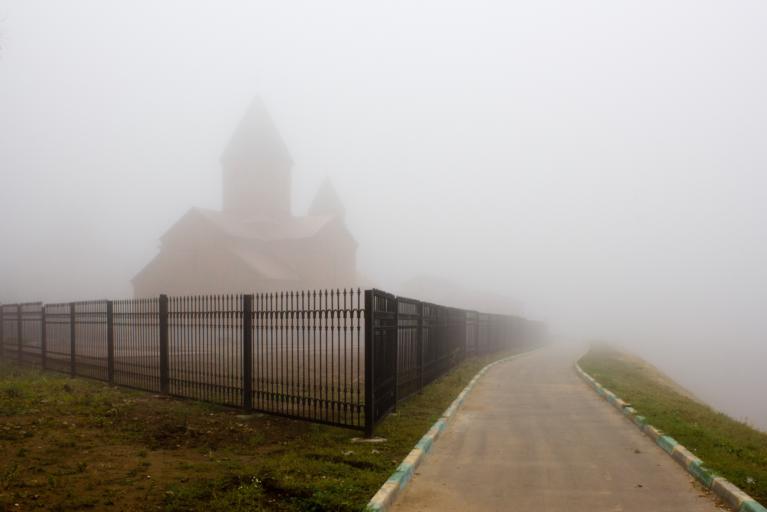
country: RU
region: Nizjnij Novgorod
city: Nizhniy Novgorod
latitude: 56.3156
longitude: 43.9797
